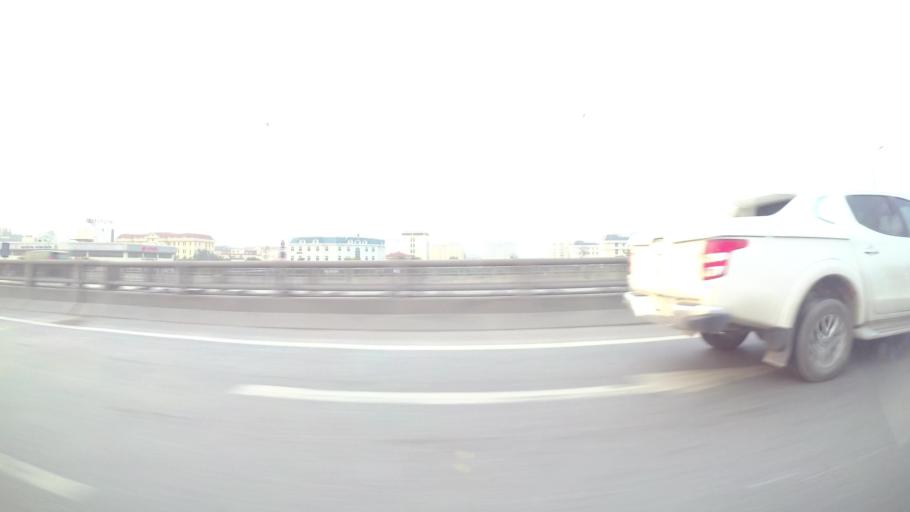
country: VN
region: Ha Noi
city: Van Dien
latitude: 20.9657
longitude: 105.8473
